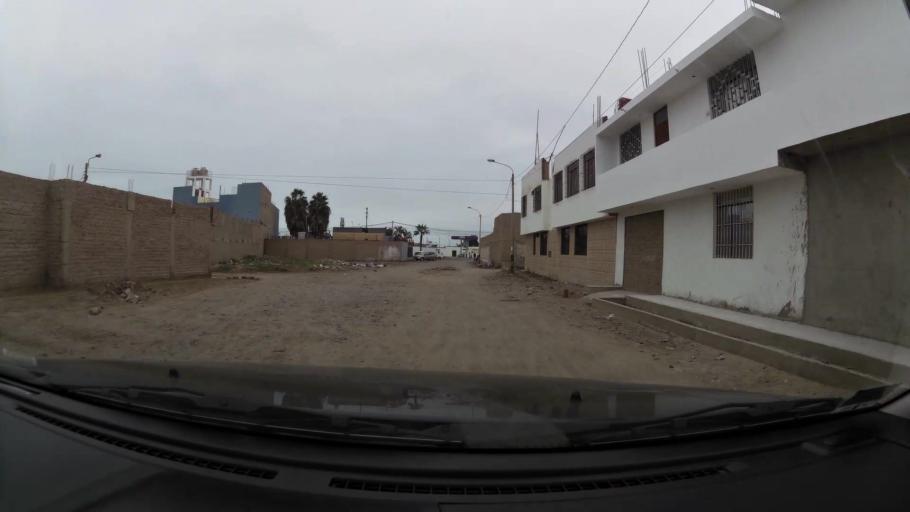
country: PE
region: Ica
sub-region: Provincia de Pisco
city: Pisco
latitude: -13.7176
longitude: -76.2125
